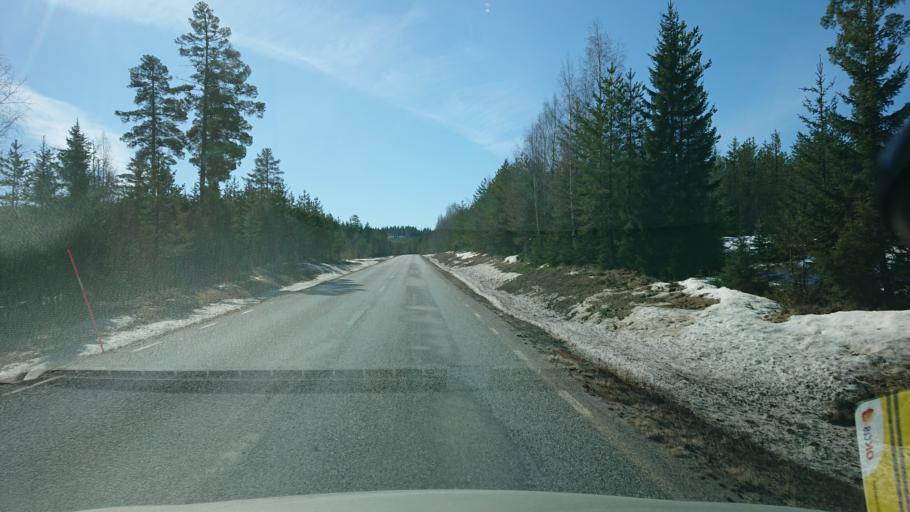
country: SE
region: Vaesterbotten
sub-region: Dorotea Kommun
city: Dorotea
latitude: 64.0024
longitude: 16.3048
